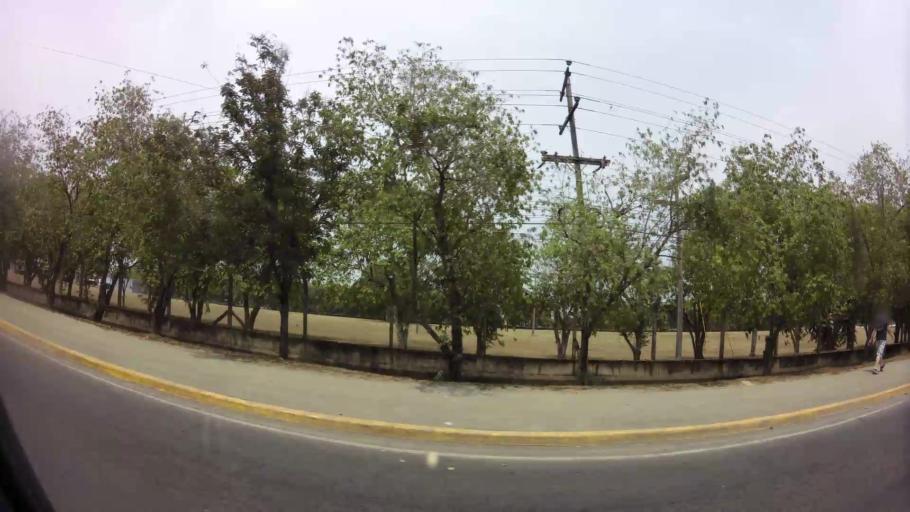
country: HN
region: Cortes
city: Villanueva
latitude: 15.3209
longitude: -87.9914
